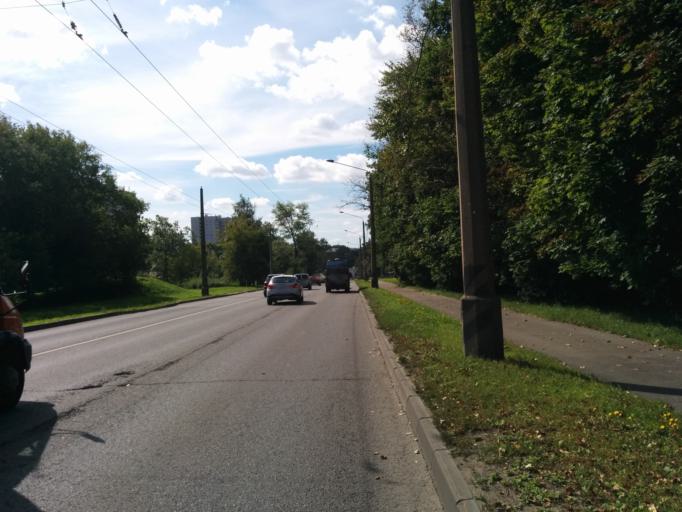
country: RU
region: Moscow
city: Ostankinskiy
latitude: 55.8158
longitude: 37.6177
